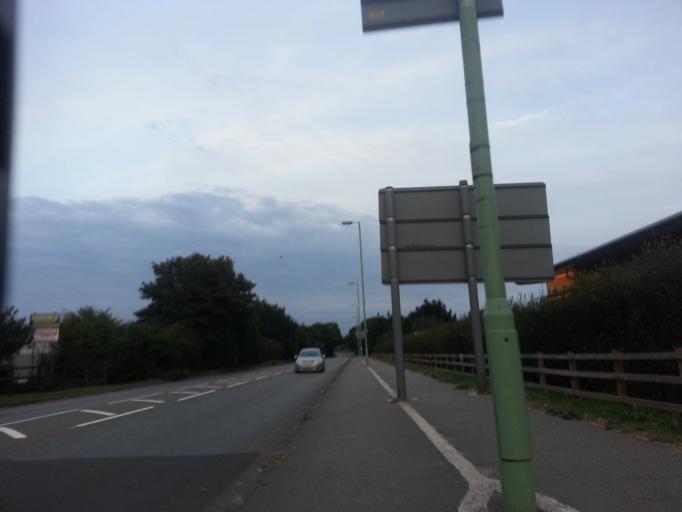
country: GB
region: England
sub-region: Suffolk
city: Kesgrave
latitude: 52.0290
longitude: 1.2028
